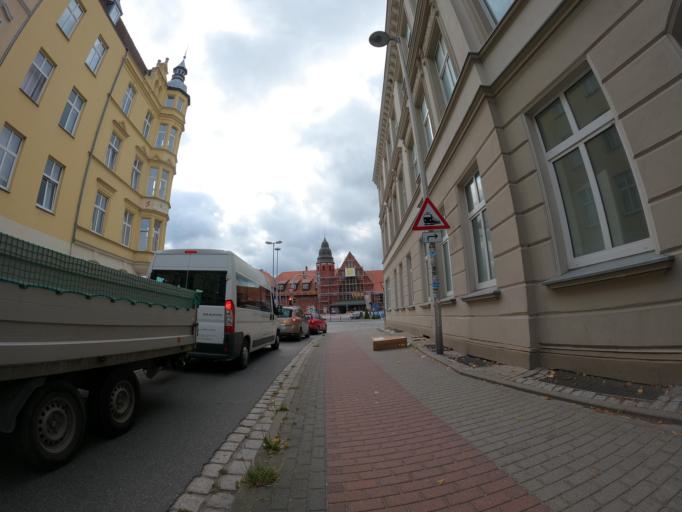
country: DE
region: Mecklenburg-Vorpommern
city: Stralsund
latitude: 54.3096
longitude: 13.0769
